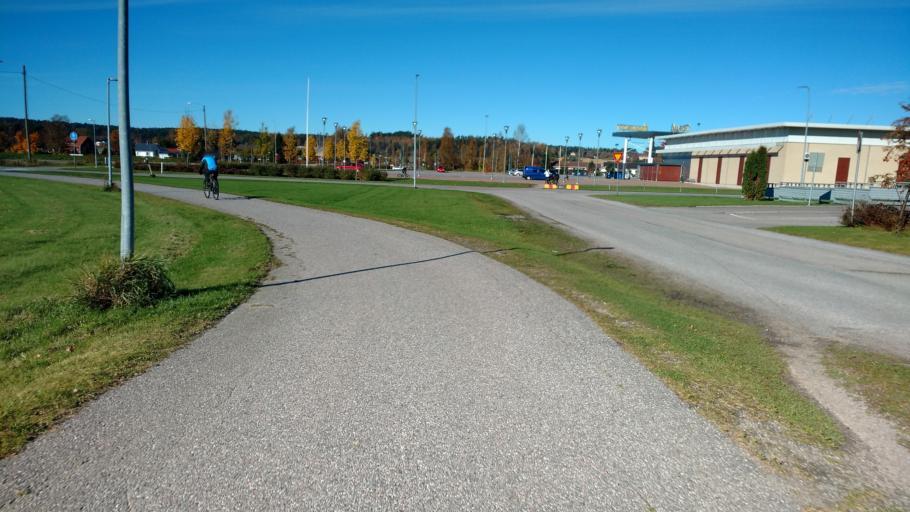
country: FI
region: Varsinais-Suomi
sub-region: Salo
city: Salo
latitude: 60.4030
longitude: 23.1722
